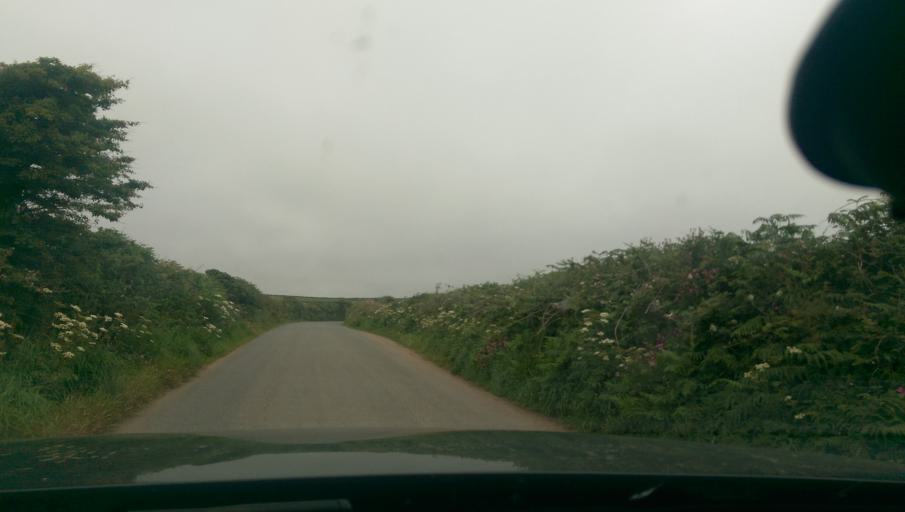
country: GB
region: England
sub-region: Cornwall
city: St. Buryan
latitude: 50.0924
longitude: -5.6442
